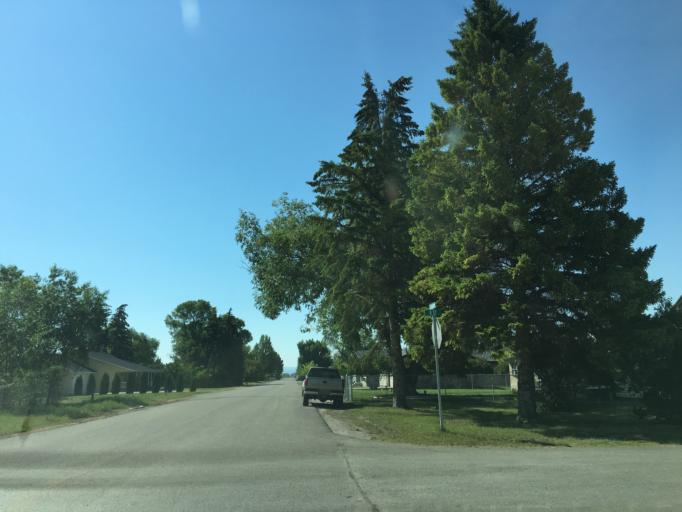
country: US
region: Montana
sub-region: Broadwater County
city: Townsend
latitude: 46.3206
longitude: -111.5128
